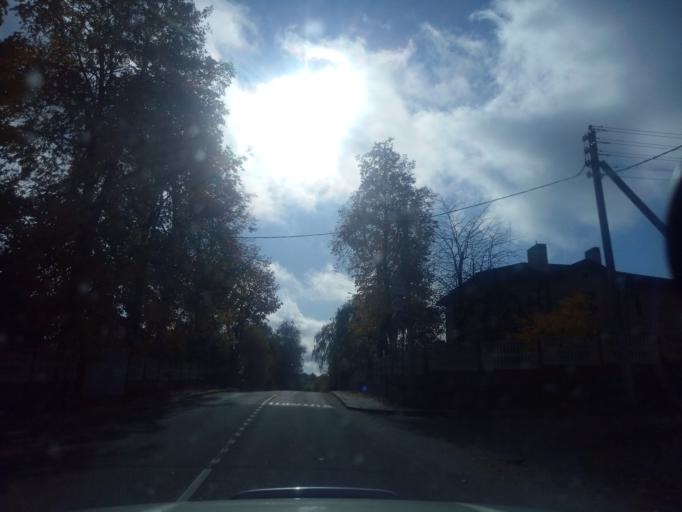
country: BY
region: Minsk
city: Zaslawye
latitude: 54.0031
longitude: 27.2925
